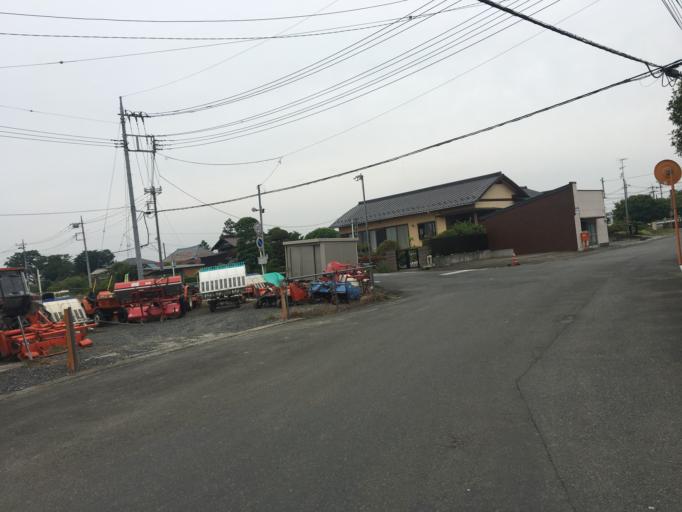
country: JP
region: Saitama
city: Sakado
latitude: 36.0020
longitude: 139.4380
